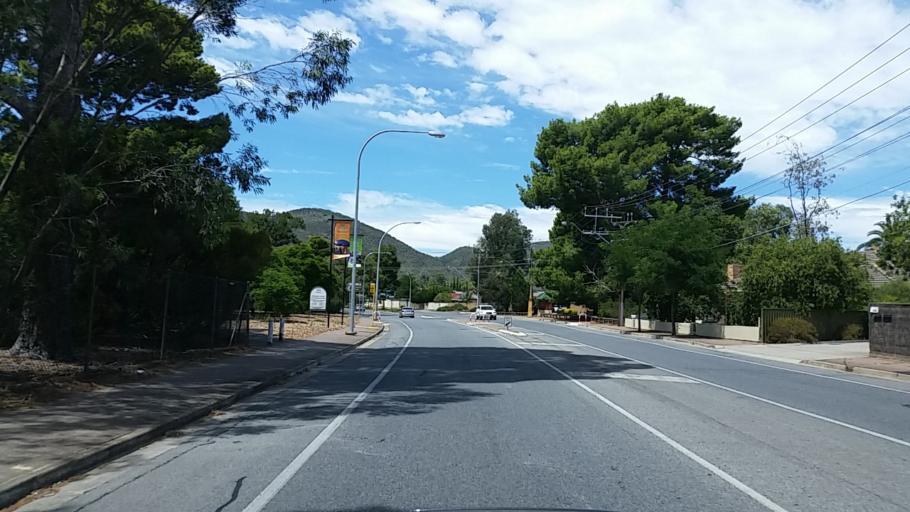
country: AU
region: South Australia
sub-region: Campbelltown
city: Athelstone
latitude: -34.8767
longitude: 138.6875
